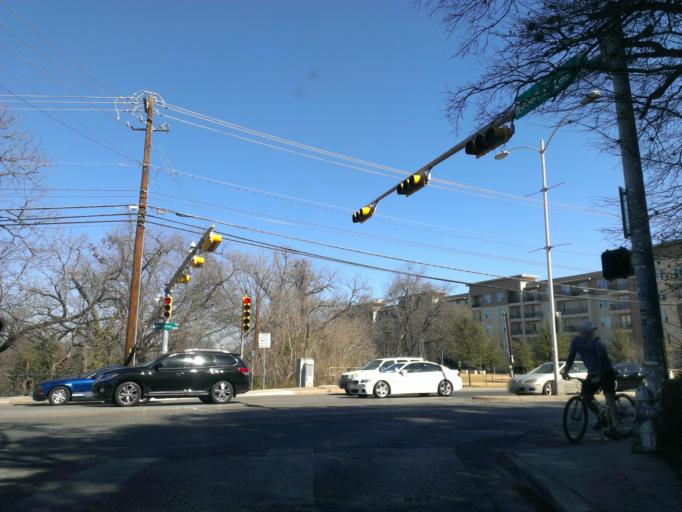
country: US
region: Texas
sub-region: Travis County
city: Austin
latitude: 30.2647
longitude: -97.7651
